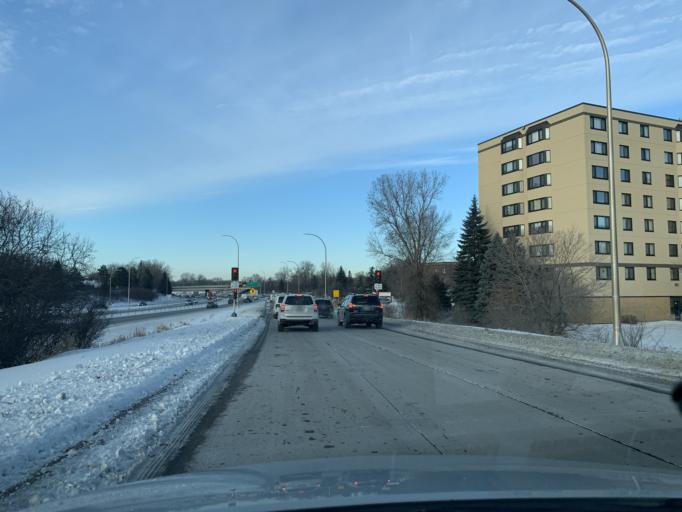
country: US
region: Minnesota
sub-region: Hennepin County
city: Minnetonka Mills
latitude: 44.9362
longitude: -93.3960
